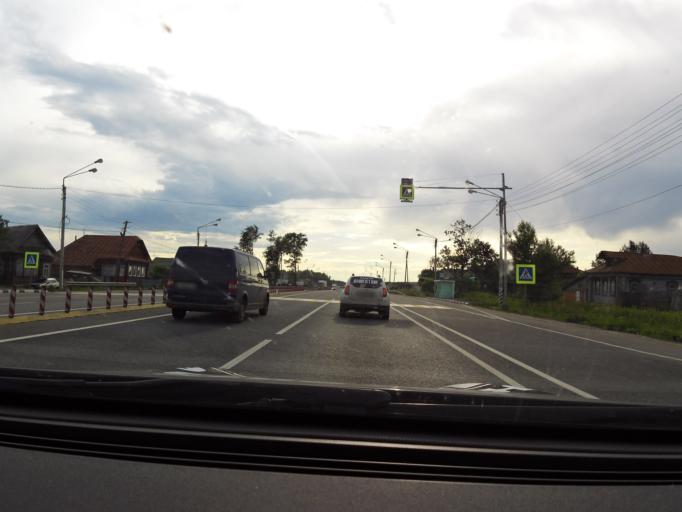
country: RU
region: Vladimir
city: Luknovo
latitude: 56.2377
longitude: 41.9915
